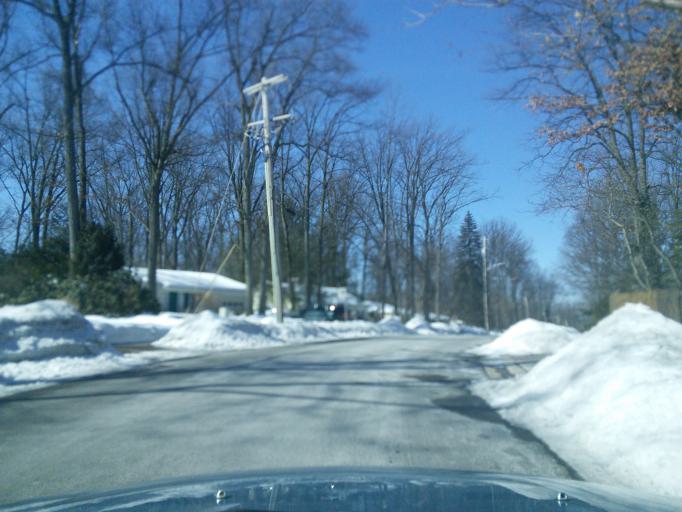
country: US
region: Pennsylvania
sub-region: Centre County
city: Park Forest Village
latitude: 40.8020
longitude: -77.9128
